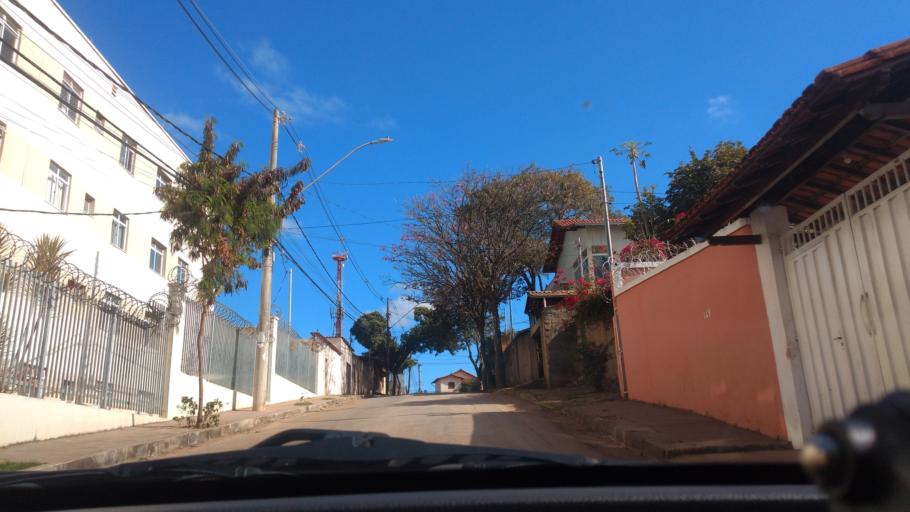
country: BR
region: Minas Gerais
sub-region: Santa Luzia
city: Santa Luzia
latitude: -19.8093
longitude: -43.9384
